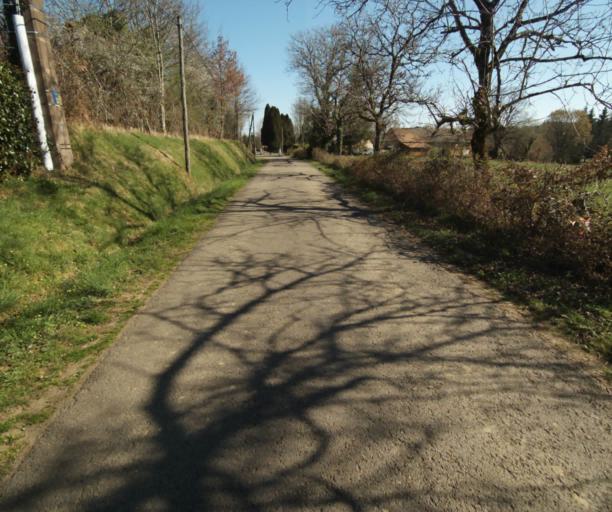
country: FR
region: Limousin
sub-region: Departement de la Correze
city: Tulle
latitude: 45.2781
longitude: 1.7222
